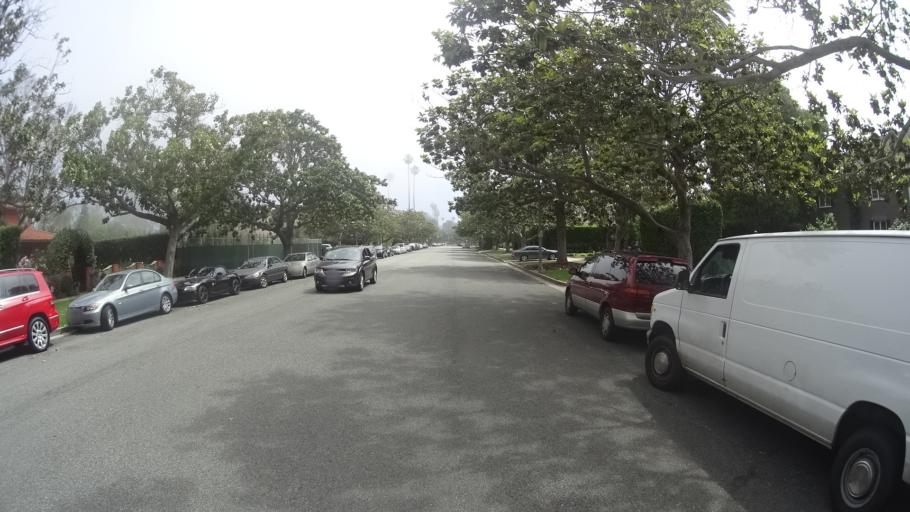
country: US
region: California
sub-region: Los Angeles County
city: Santa Monica
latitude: 34.0243
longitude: -118.5070
